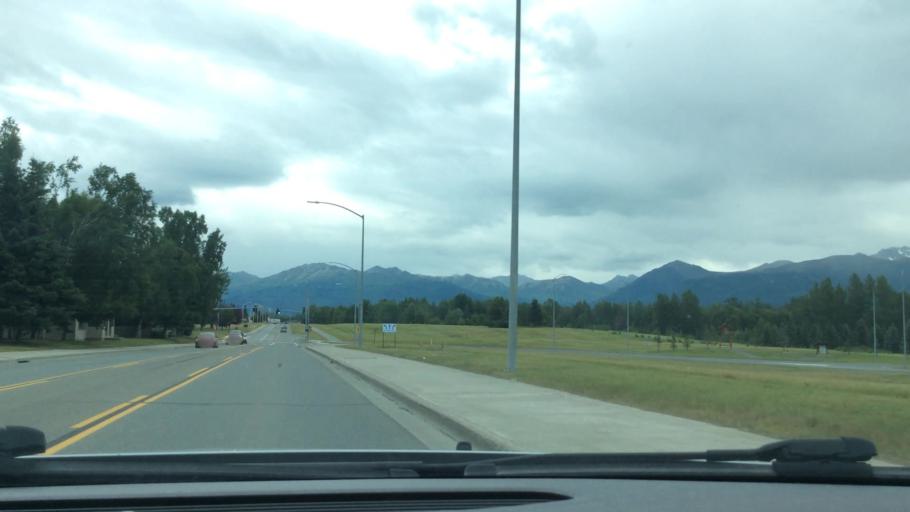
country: US
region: Alaska
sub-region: Anchorage Municipality
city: Anchorage
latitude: 61.2379
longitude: -149.8200
